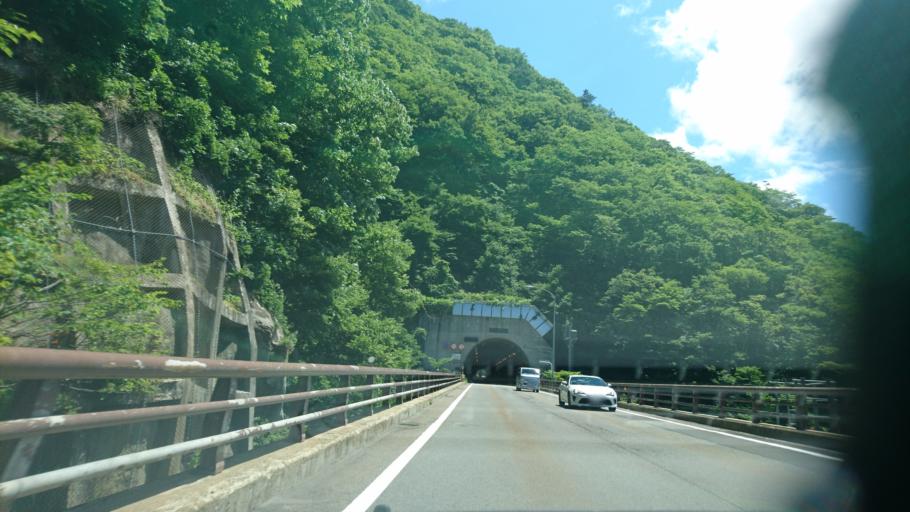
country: JP
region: Iwate
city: Shizukuishi
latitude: 39.7004
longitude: 140.7659
